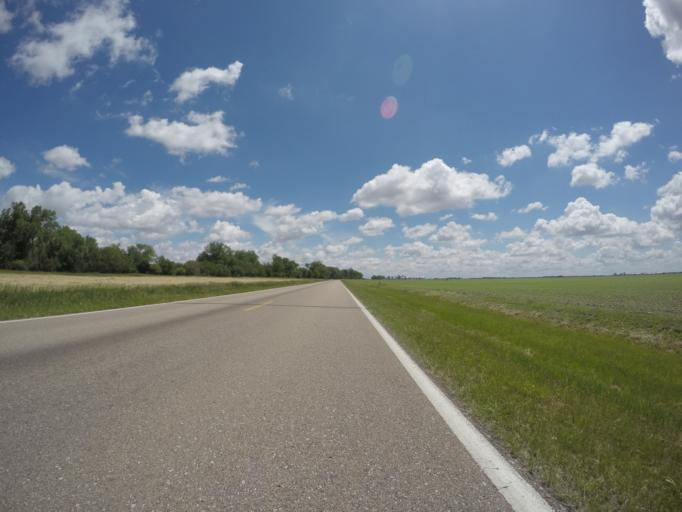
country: US
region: Nebraska
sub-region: Buffalo County
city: Kearney
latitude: 40.6557
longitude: -99.1356
